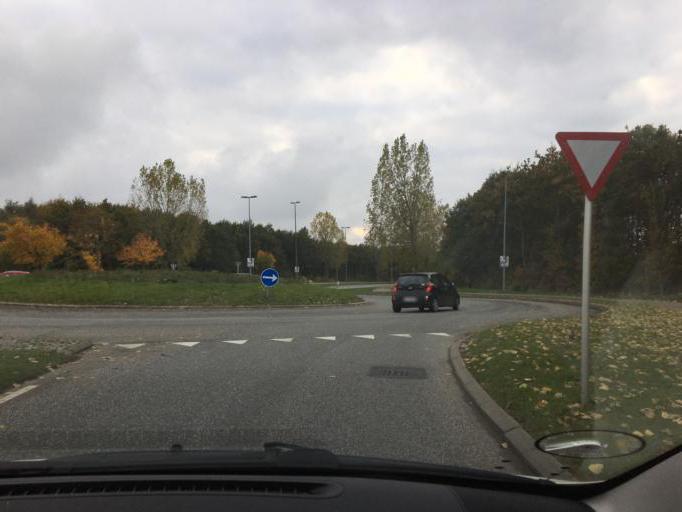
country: DK
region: South Denmark
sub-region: Fredericia Kommune
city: Fredericia
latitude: 55.5887
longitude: 9.7537
